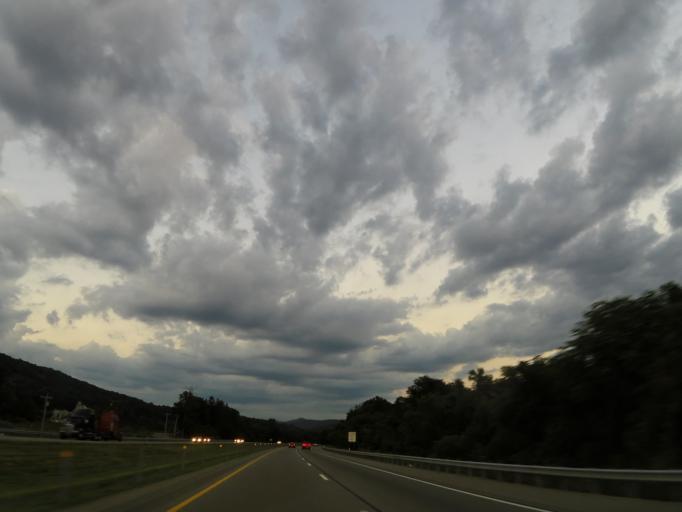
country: US
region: Tennessee
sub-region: Putnam County
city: Algood
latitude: 36.1384
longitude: -85.4411
